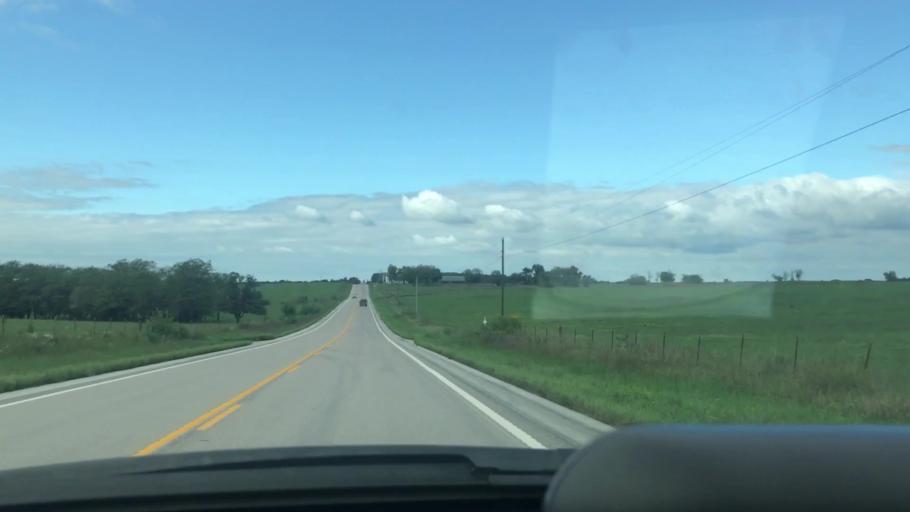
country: US
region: Missouri
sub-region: Hickory County
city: Hermitage
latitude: 37.9490
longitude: -93.2076
